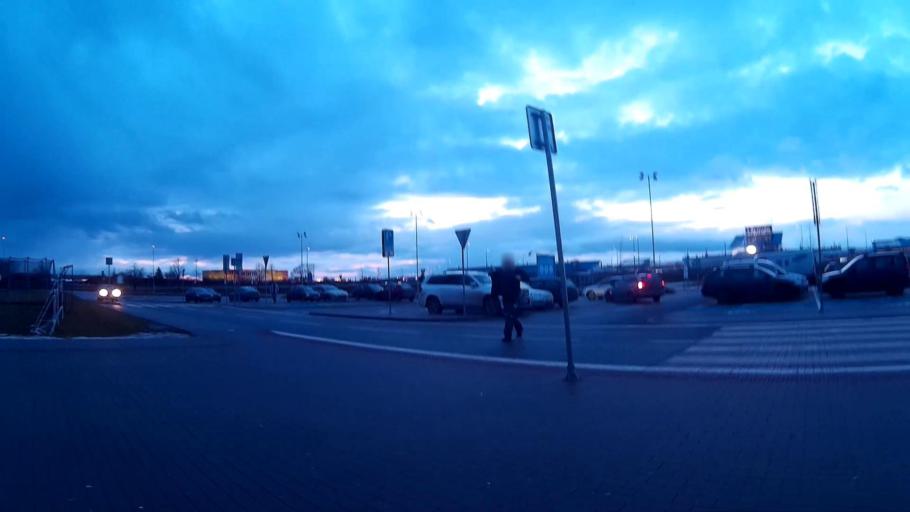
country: CZ
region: South Moravian
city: Modrice
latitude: 49.1378
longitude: 16.6378
